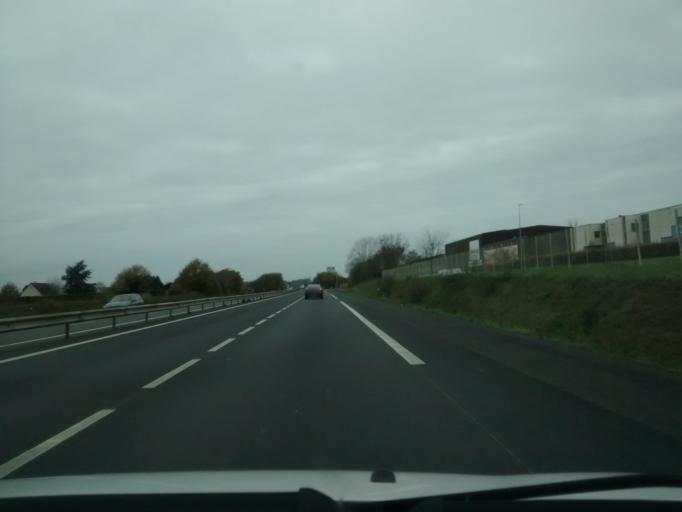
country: FR
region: Brittany
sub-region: Departement d'Ille-et-Vilaine
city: Torce
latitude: 48.0749
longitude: -1.2618
